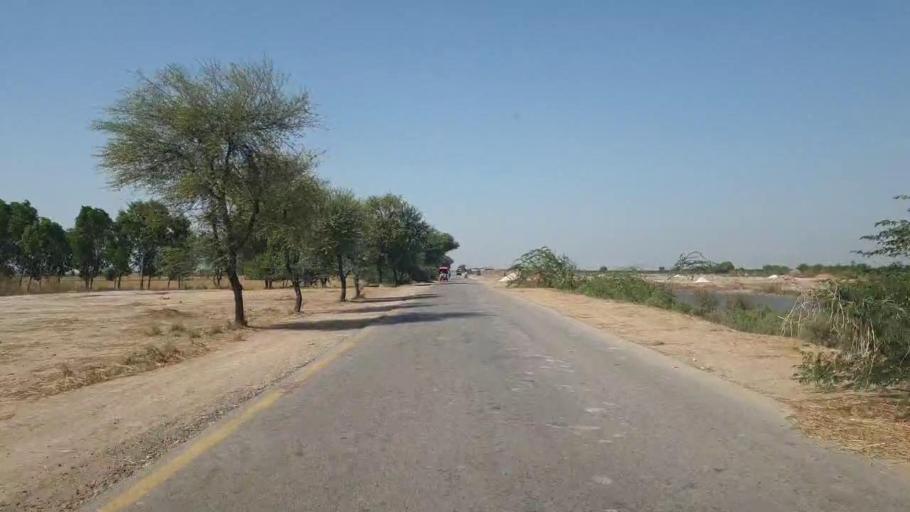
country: PK
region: Sindh
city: Rajo Khanani
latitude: 25.0078
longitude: 68.8355
